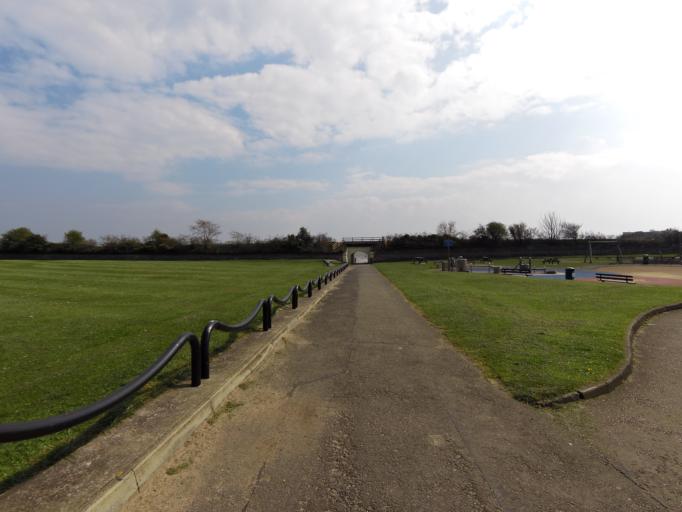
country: GB
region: Scotland
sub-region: Fife
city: Burntisland
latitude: 56.0627
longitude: -3.2244
